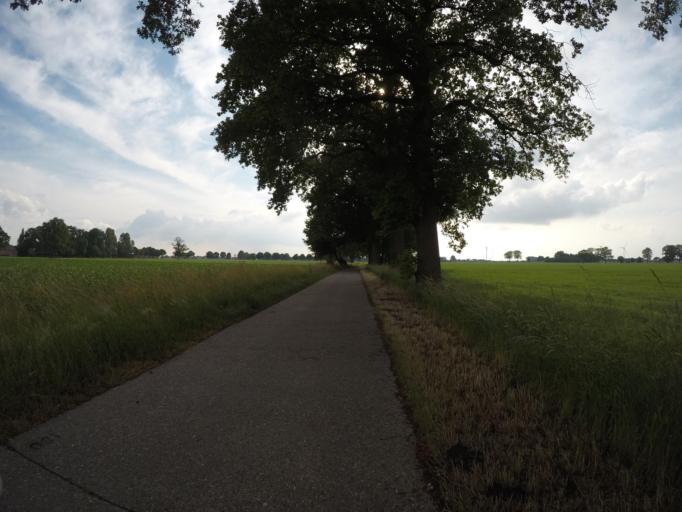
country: BE
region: Flanders
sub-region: Provincie Antwerpen
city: Brecht
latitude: 51.3595
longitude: 4.6839
